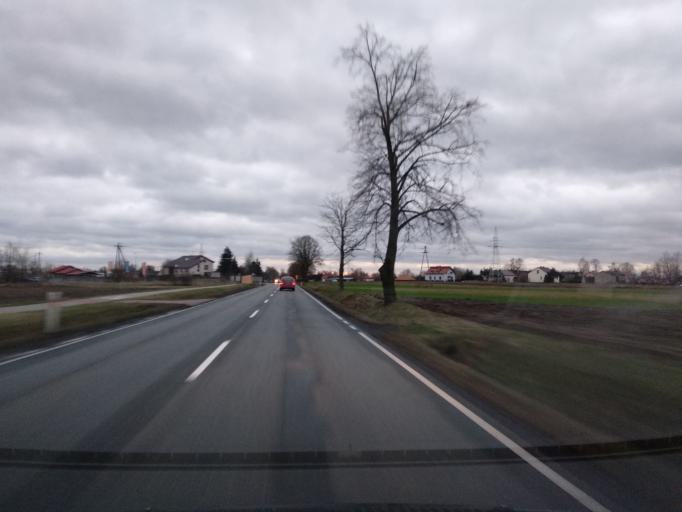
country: PL
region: Greater Poland Voivodeship
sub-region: Powiat koninski
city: Rychwal
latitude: 52.0835
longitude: 18.1622
